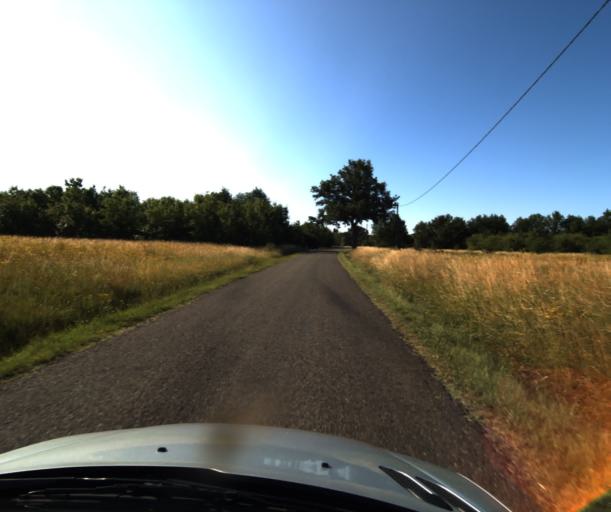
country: FR
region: Midi-Pyrenees
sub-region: Departement du Tarn-et-Garonne
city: Saint-Porquier
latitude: 44.0532
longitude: 1.2116
